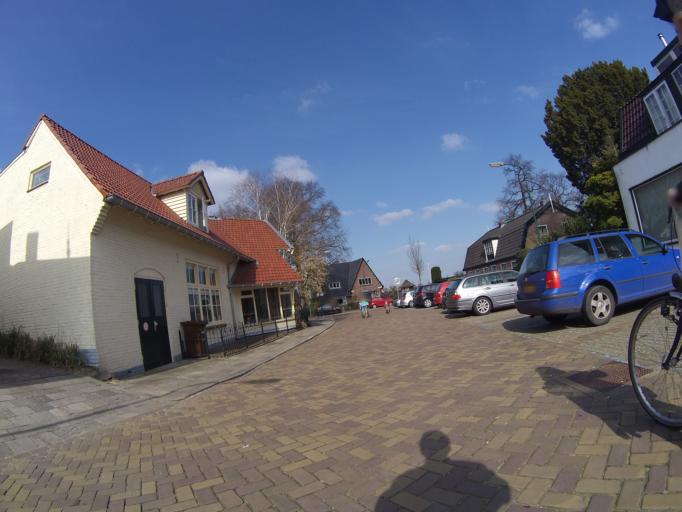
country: NL
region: Utrecht
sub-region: Gemeente Soest
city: Soest
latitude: 52.1861
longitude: 5.2977
